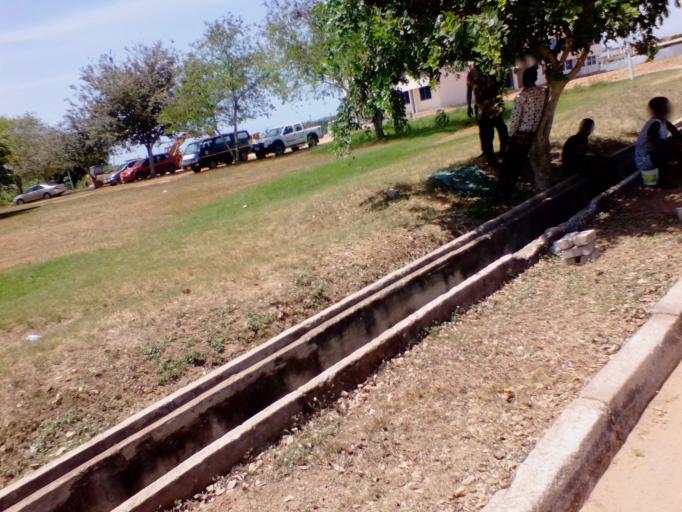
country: GH
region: Central
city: Cape Coast
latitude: 5.1212
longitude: -1.2939
